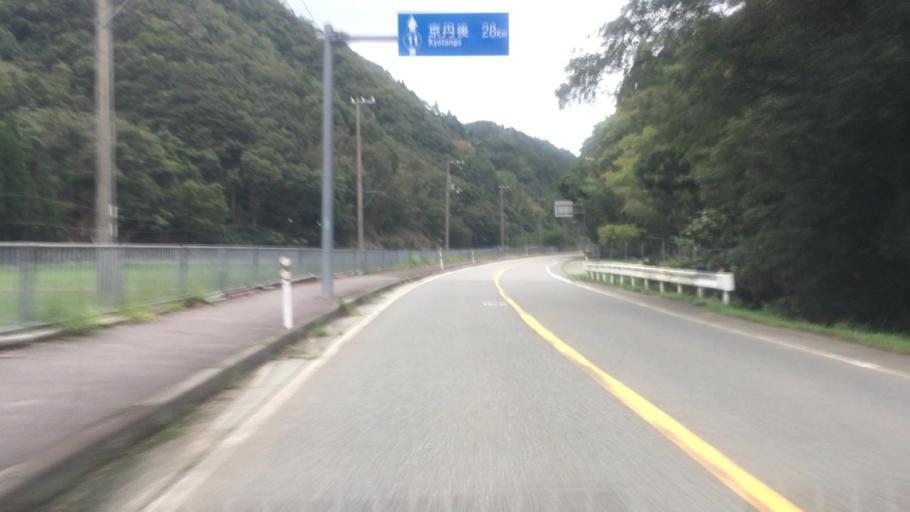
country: JP
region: Hyogo
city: Toyooka
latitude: 35.6153
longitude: 134.8462
